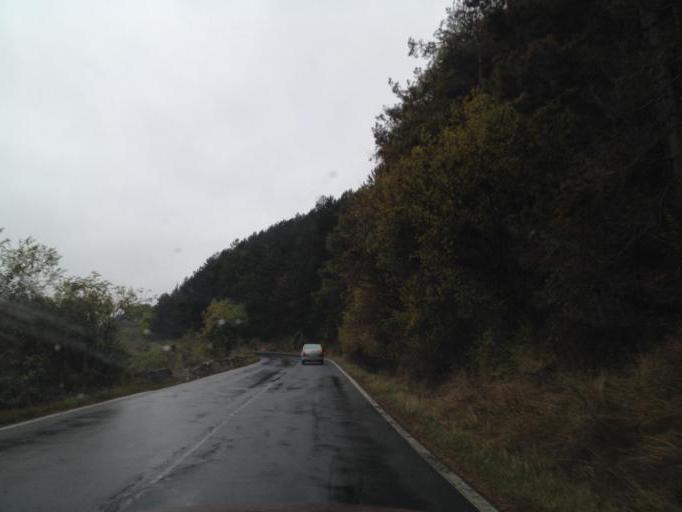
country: RO
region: Arges
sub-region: Comuna Stoenesti
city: Stoenesti
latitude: 45.2971
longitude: 25.1447
